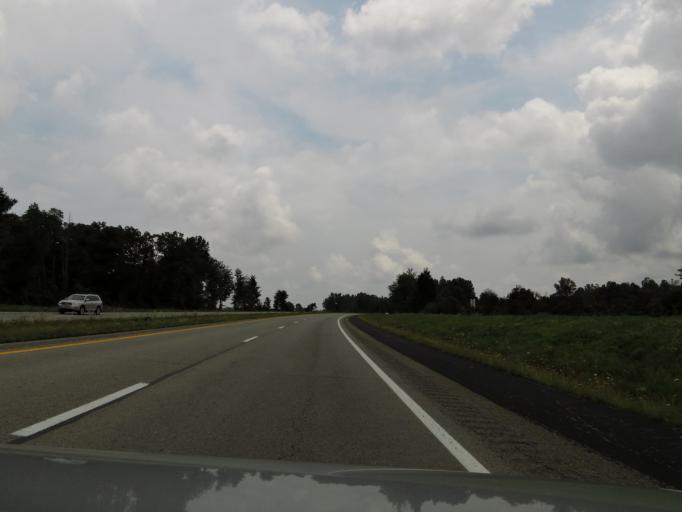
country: US
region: Kentucky
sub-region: Grayson County
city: Leitchfield
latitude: 37.5488
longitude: -86.1205
